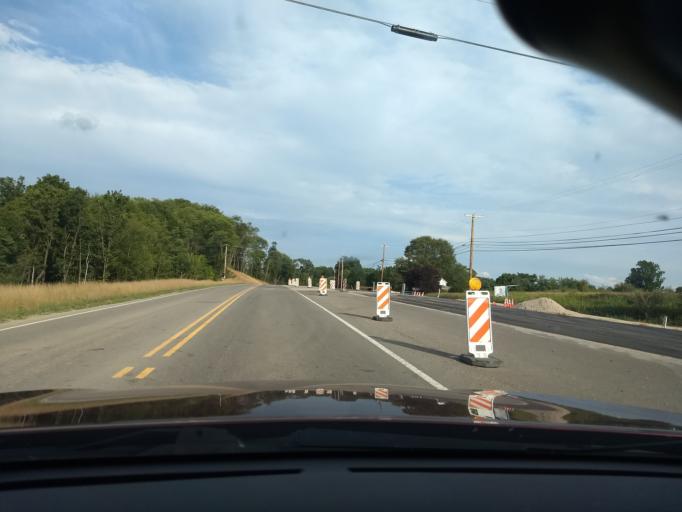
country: US
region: Pennsylvania
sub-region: Armstrong County
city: Freeport
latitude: 40.6620
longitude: -79.6771
